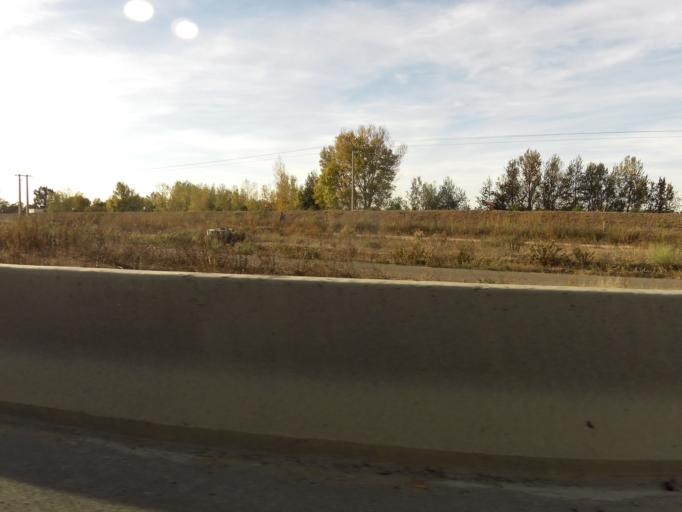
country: FR
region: Languedoc-Roussillon
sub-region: Departement du Gard
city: Aimargues
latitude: 43.7078
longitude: 4.2127
